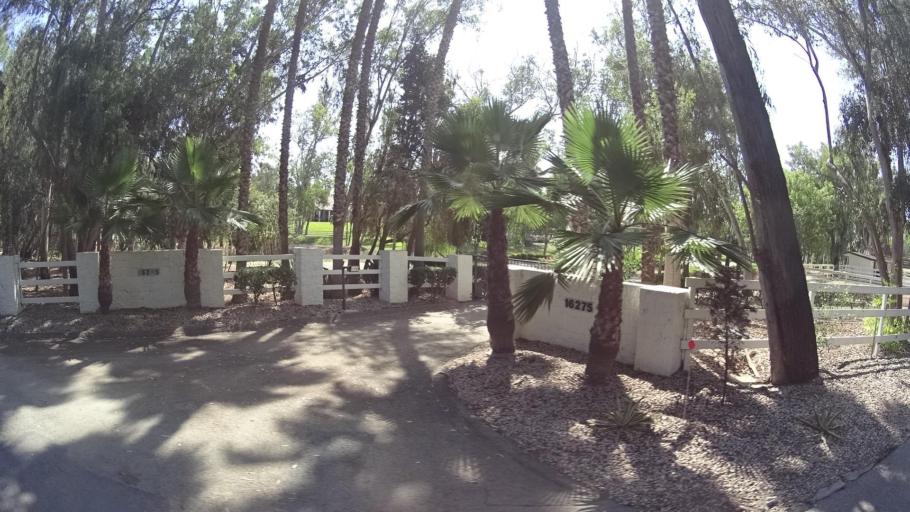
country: US
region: California
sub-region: San Diego County
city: Rancho Santa Fe
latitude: 33.0104
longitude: -117.2037
